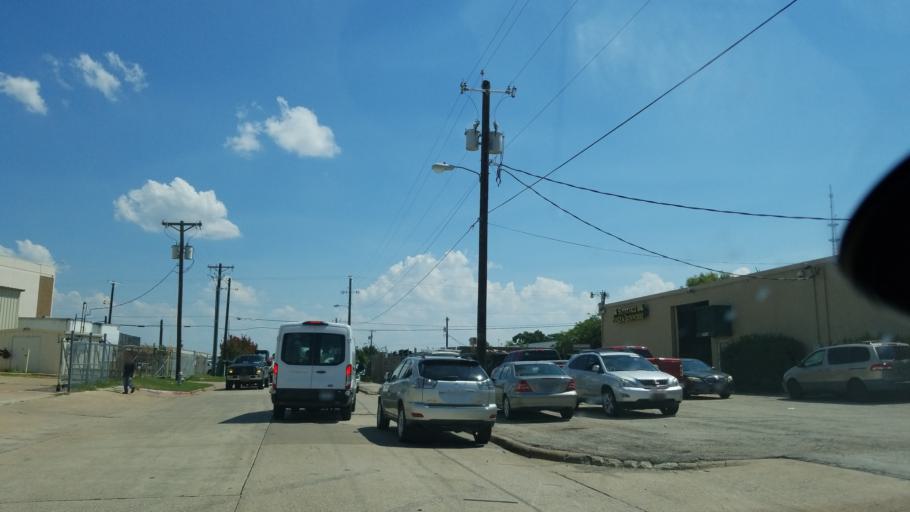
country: US
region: Texas
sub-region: Dallas County
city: Richardson
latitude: 32.9038
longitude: -96.6951
